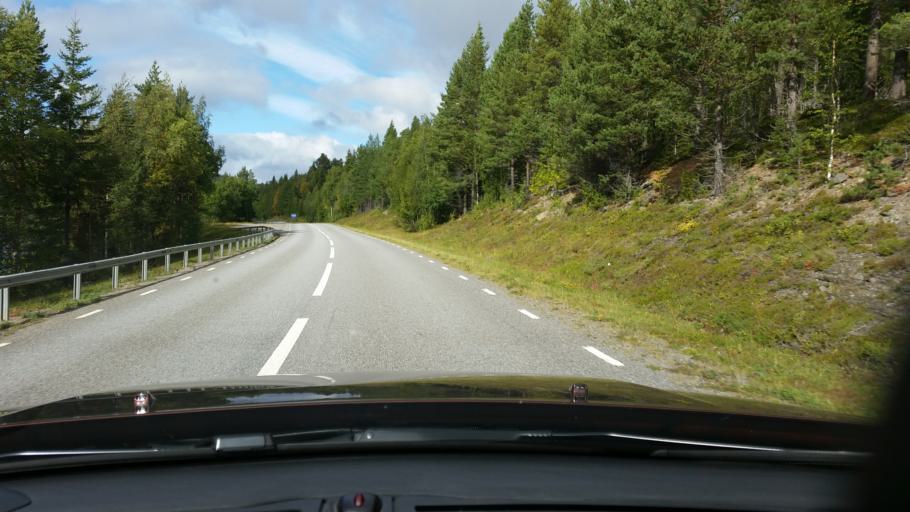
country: SE
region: Jaemtland
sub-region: Stroemsunds Kommun
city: Stroemsund
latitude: 64.3696
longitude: 14.6597
